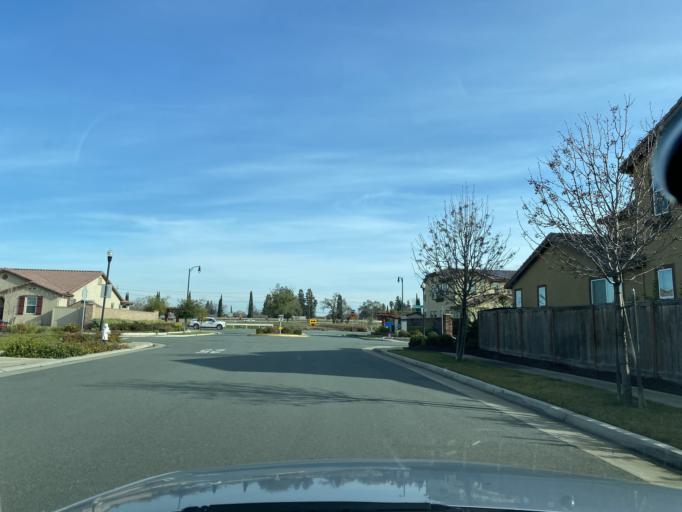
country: US
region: California
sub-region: Sacramento County
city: Elk Grove
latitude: 38.3977
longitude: -121.3847
